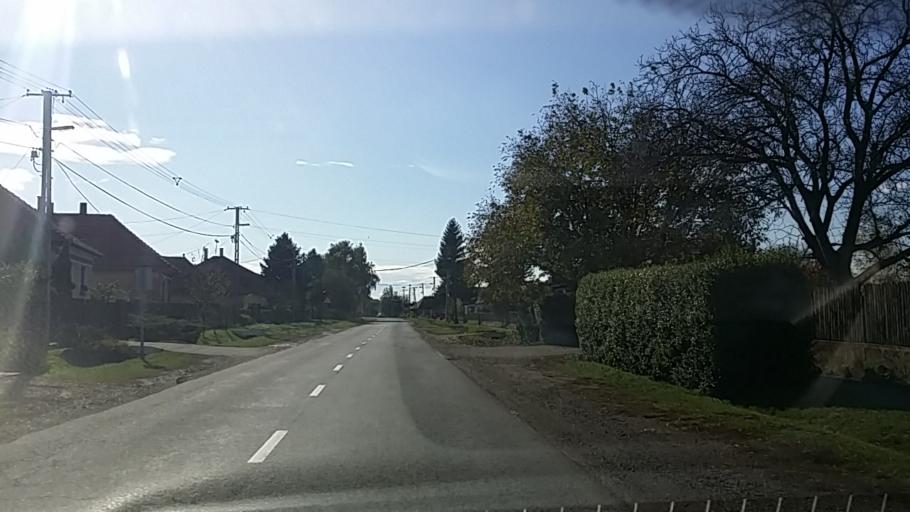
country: HU
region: Borsod-Abauj-Zemplen
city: Gonc
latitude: 48.4222
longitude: 21.2349
